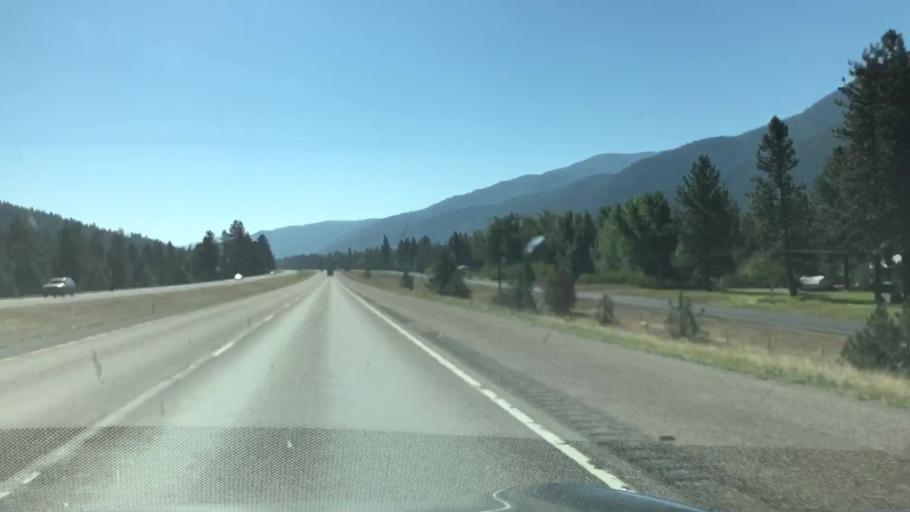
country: US
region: Montana
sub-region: Missoula County
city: Bonner-West Riverside
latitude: 46.8563
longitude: -113.8629
